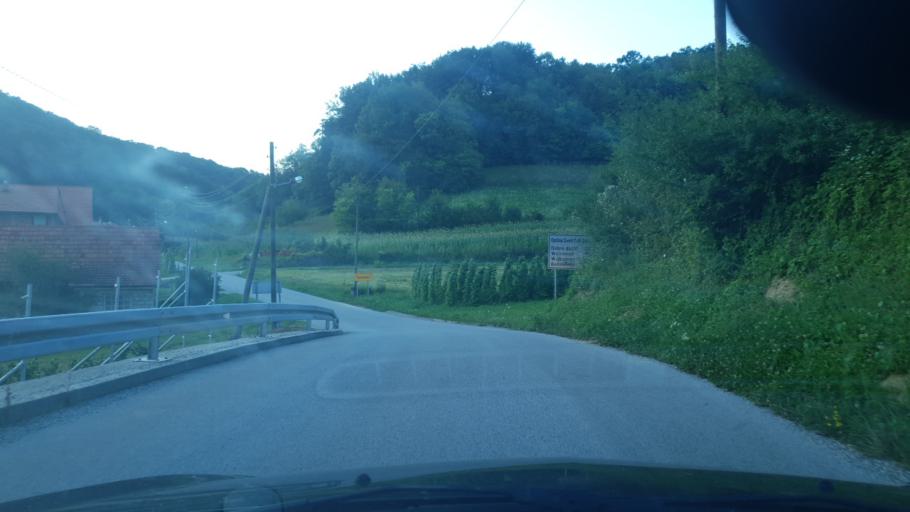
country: HR
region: Krapinsko-Zagorska
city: Zabok
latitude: 46.0444
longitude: 15.8877
